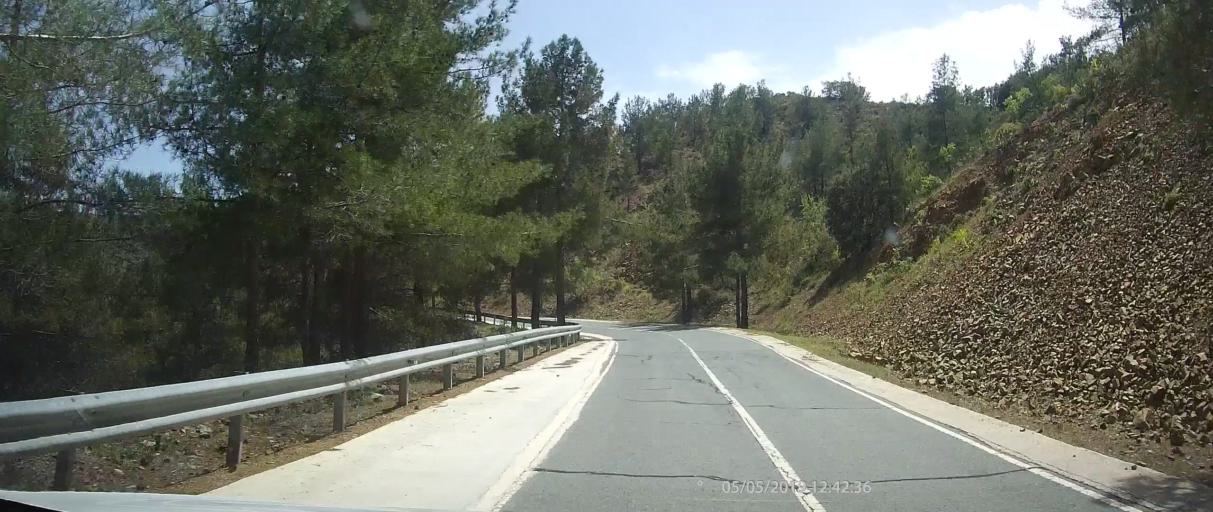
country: CY
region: Lefkosia
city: Kakopetria
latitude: 34.9729
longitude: 32.8113
